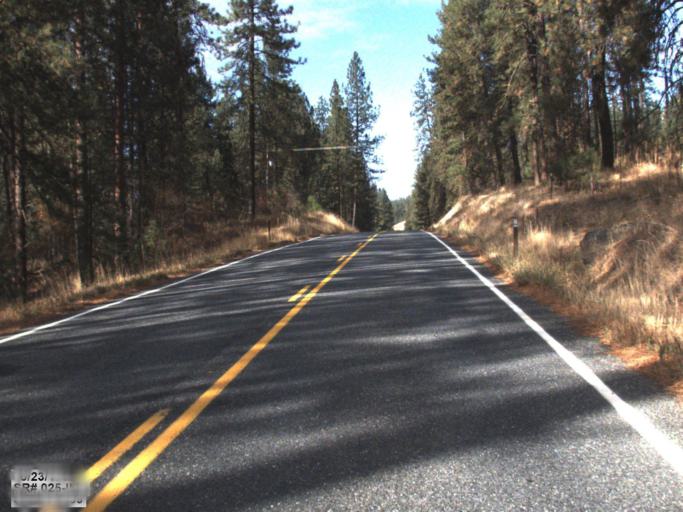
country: US
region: Washington
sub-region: Stevens County
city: Kettle Falls
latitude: 48.2711
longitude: -118.1338
